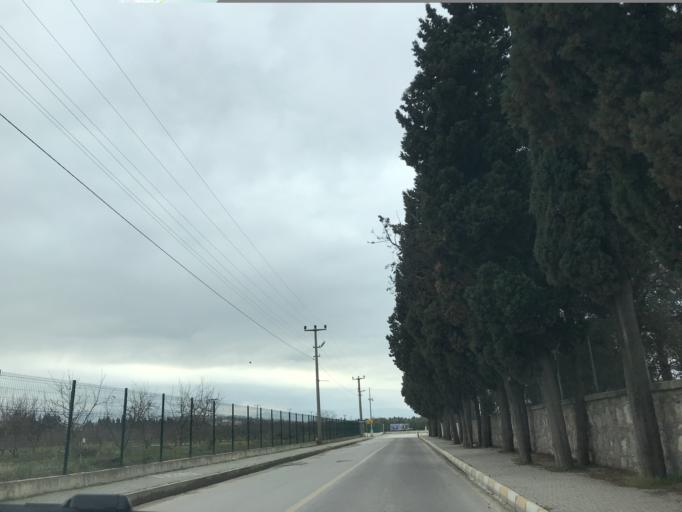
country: TR
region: Yalova
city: Ciftlikkoy
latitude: 40.6635
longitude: 29.3035
